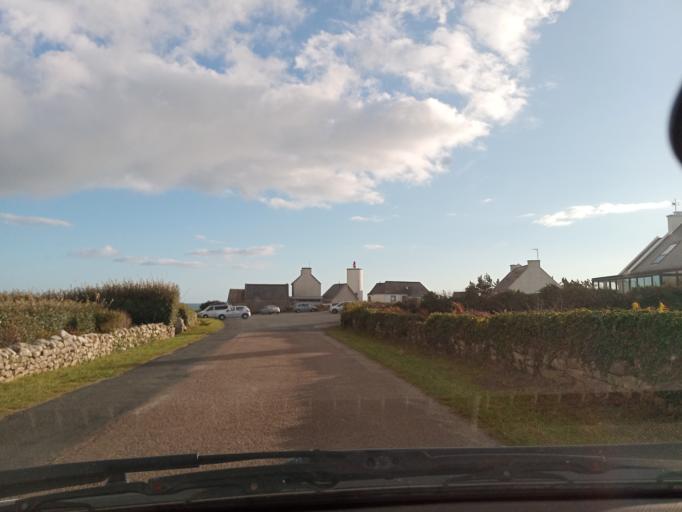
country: FR
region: Brittany
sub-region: Departement du Finistere
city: Esquibien
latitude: 48.0020
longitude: -4.5654
